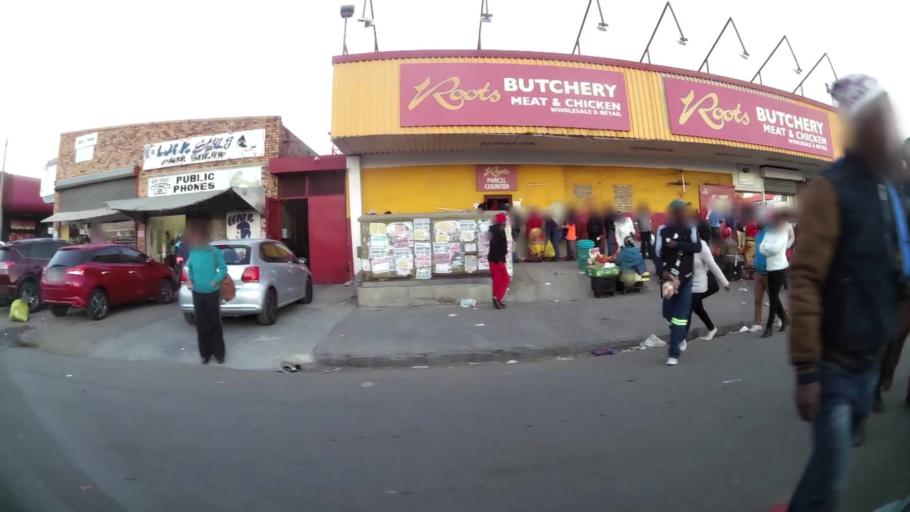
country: ZA
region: North-West
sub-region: Bojanala Platinum District Municipality
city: Rustenburg
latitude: -25.6629
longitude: 27.2375
